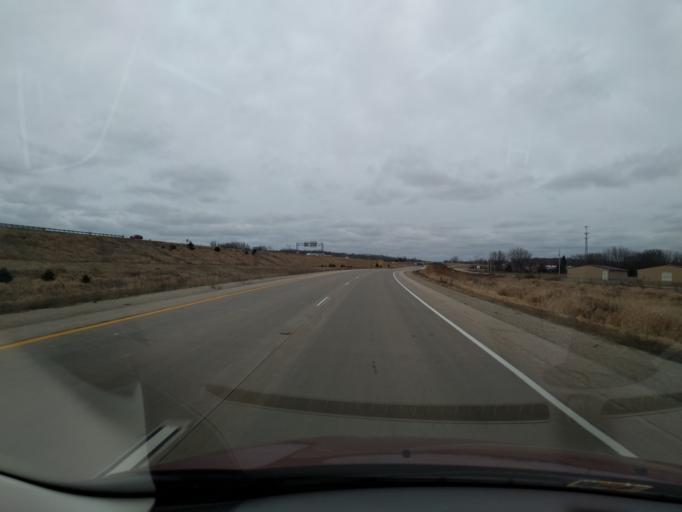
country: US
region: Wisconsin
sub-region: Winnebago County
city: Winneconne
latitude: 44.2066
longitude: -88.6842
